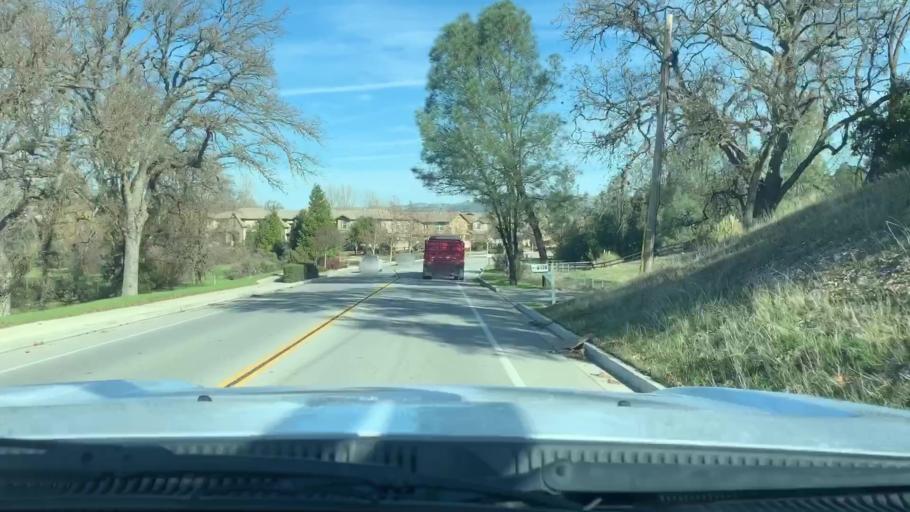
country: US
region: California
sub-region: San Luis Obispo County
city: Atascadero
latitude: 35.4447
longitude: -120.6370
